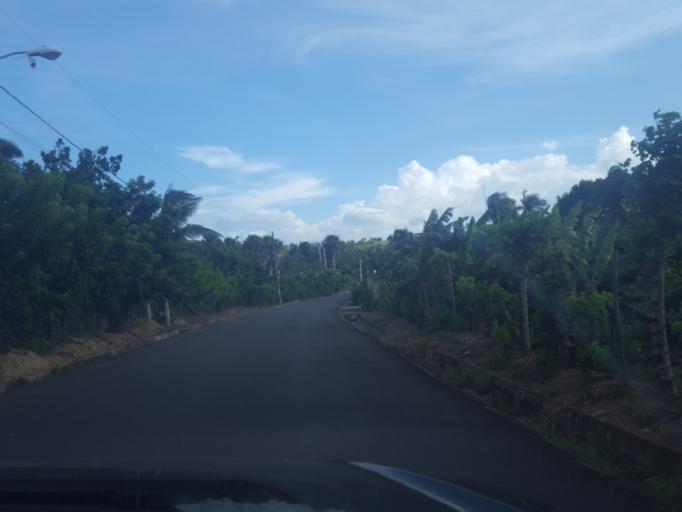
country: DO
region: Santiago
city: Licey al Medio
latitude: 19.3619
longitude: -70.6326
